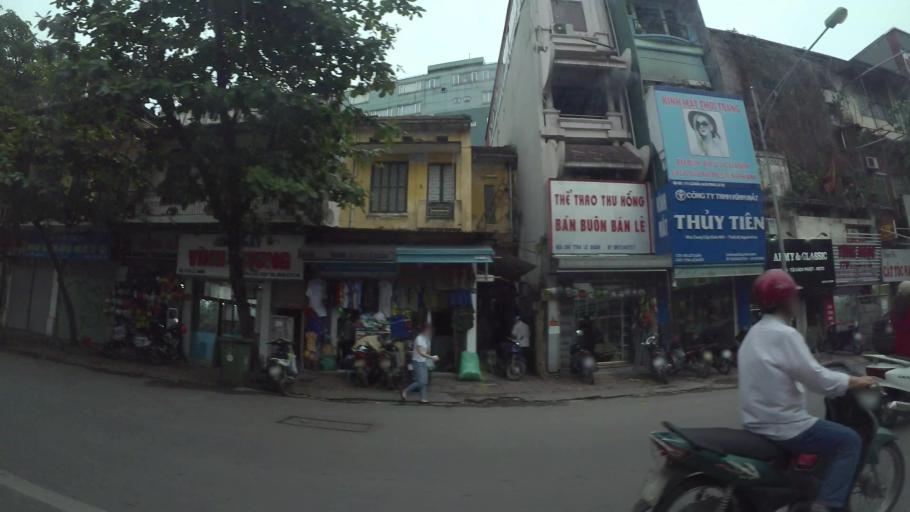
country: VN
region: Ha Noi
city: Hanoi
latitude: 21.0202
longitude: 105.8414
